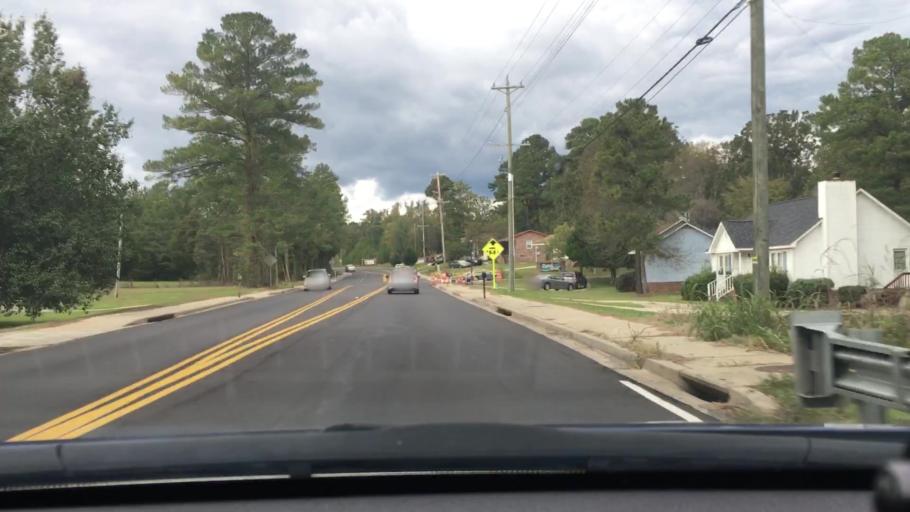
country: US
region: South Carolina
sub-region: Lexington County
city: Irmo
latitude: 34.1116
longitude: -81.1616
